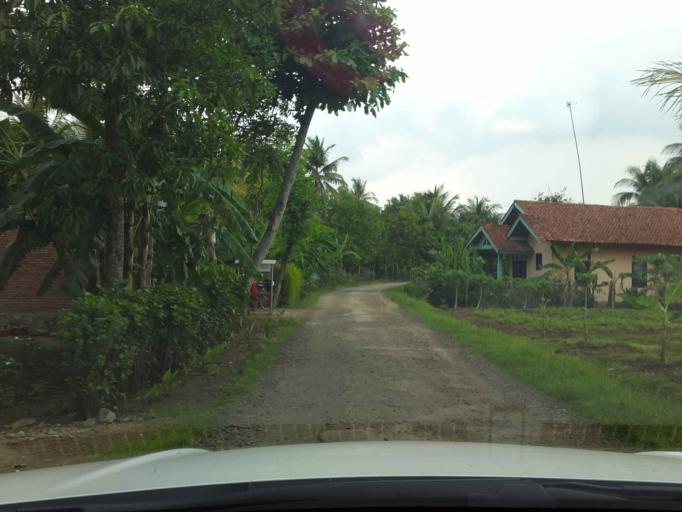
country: ID
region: West Java
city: Sarimukti Kaler
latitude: -7.4225
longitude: 108.7249
